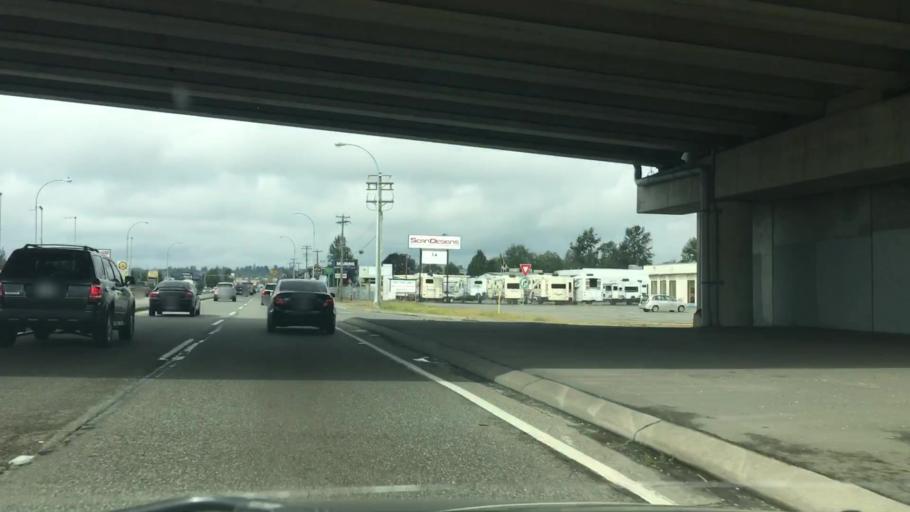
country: CA
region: British Columbia
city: Langley
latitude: 49.1133
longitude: -122.6567
